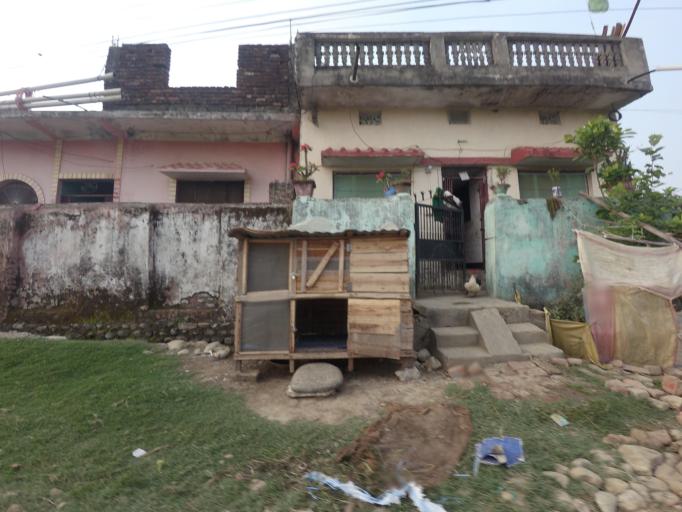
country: NP
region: Western Region
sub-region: Lumbini Zone
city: Bhairahawa
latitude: 27.5034
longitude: 83.4444
